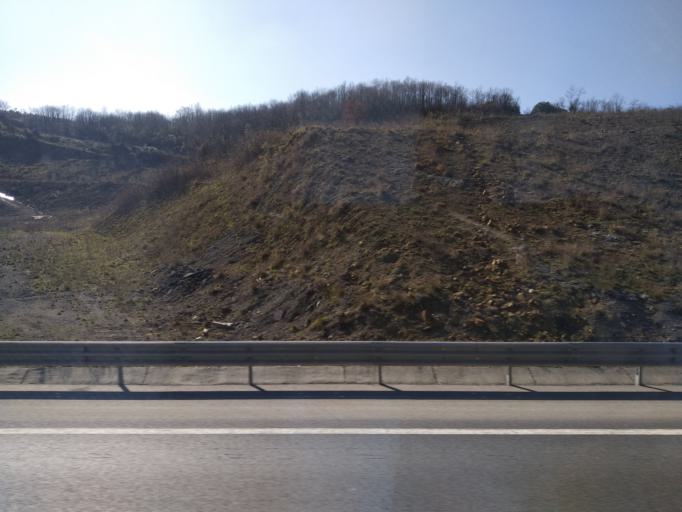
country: TR
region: Istanbul
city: Mahmut Sevket Pasa
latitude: 41.1587
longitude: 29.2623
